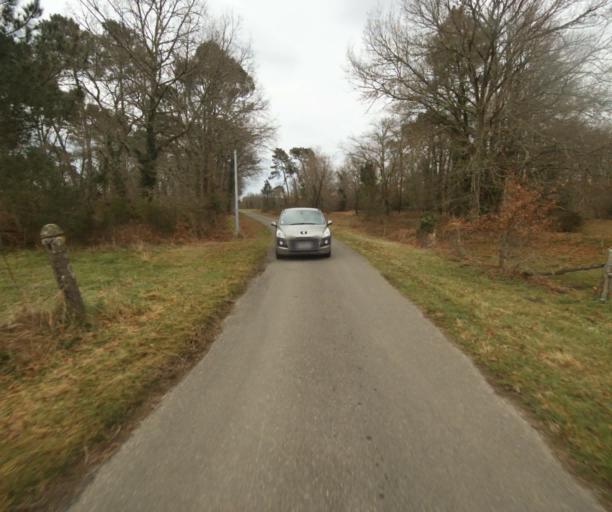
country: FR
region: Aquitaine
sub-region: Departement des Landes
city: Gabarret
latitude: 44.0187
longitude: -0.0631
